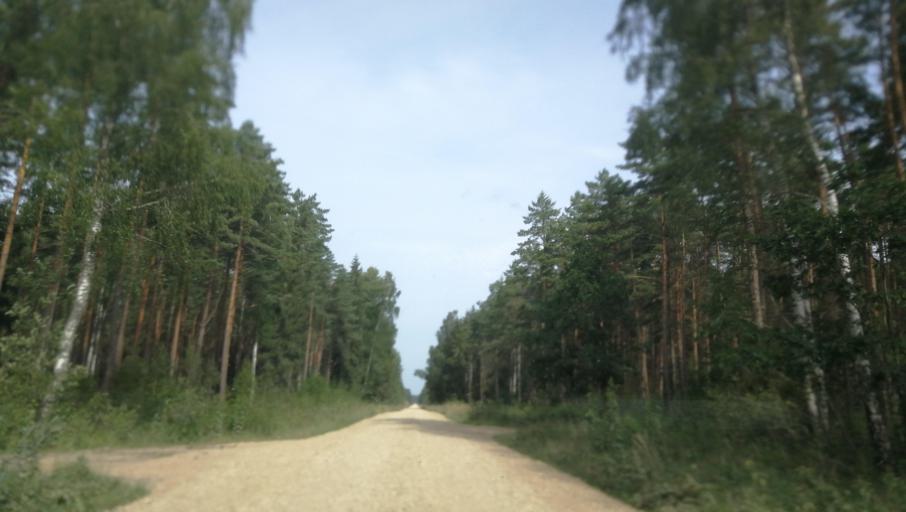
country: LV
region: Durbe
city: Liegi
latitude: 56.7573
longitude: 21.3569
